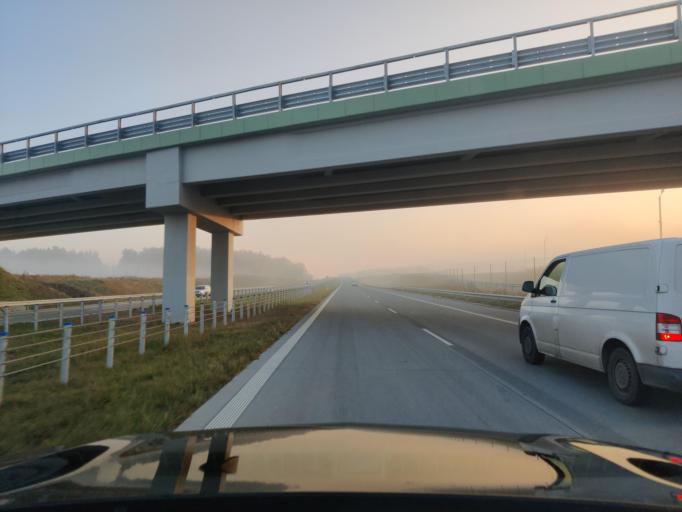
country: PL
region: Masovian Voivodeship
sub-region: Powiat mlawski
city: Strzegowo
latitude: 52.9737
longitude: 20.3265
